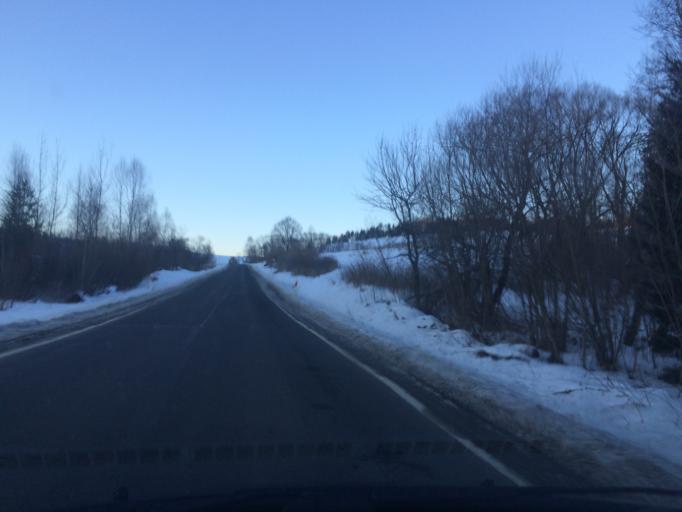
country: PL
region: Subcarpathian Voivodeship
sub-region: Powiat bieszczadzki
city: Lutowiska
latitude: 49.2327
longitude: 22.7015
